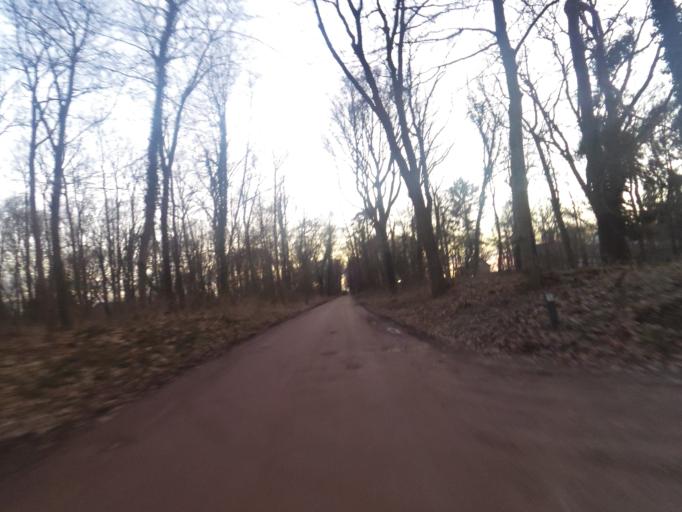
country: NL
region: Gelderland
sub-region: Gemeente Doetinchem
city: Doetinchem
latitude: 51.9385
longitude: 6.3308
